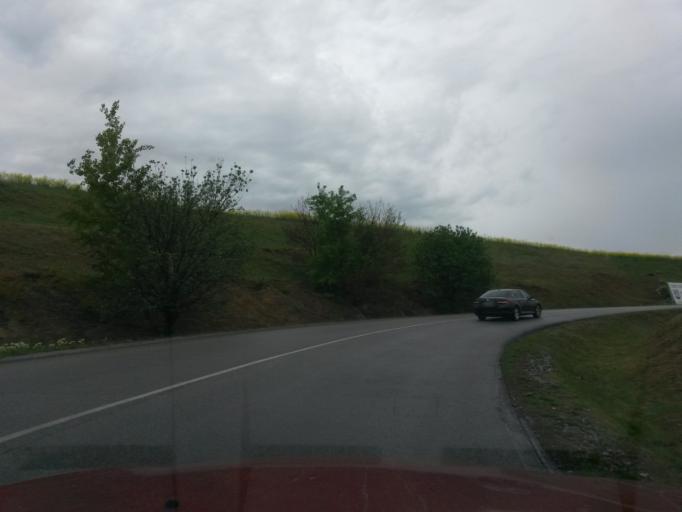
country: HU
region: Borsod-Abauj-Zemplen
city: Gonc
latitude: 48.5495
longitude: 21.2598
